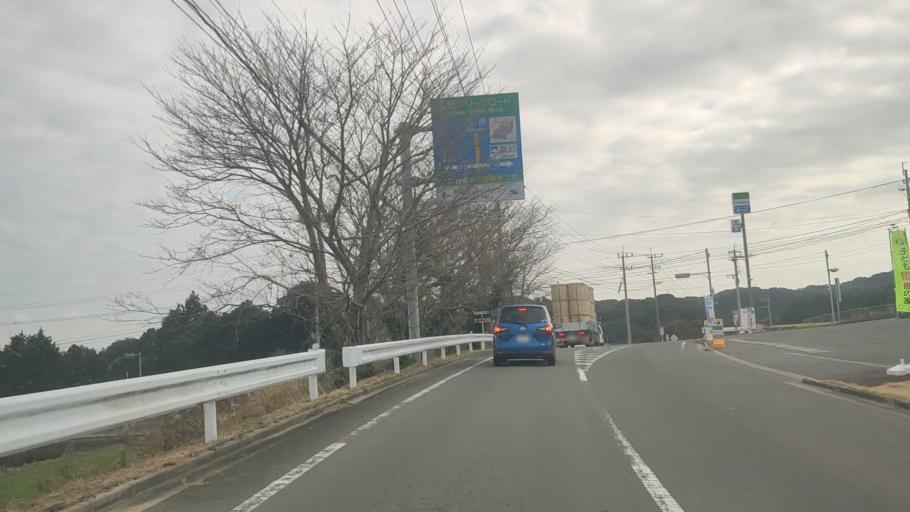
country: JP
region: Nagasaki
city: Shimabara
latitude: 32.8531
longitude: 130.2608
